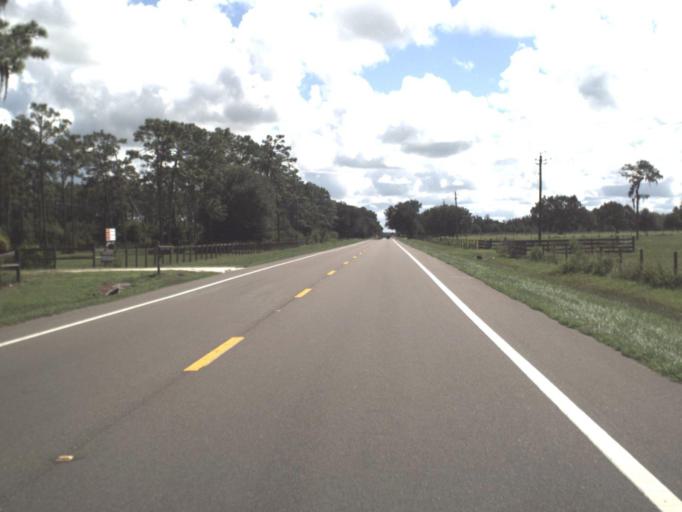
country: US
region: Florida
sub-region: Sarasota County
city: Lake Sarasota
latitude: 27.3764
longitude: -82.2282
